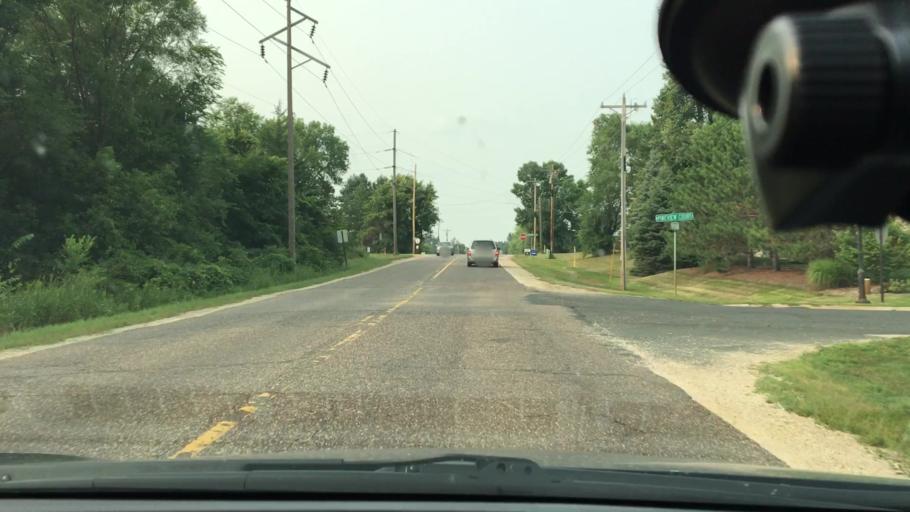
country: US
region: Minnesota
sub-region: Hennepin County
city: Champlin
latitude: 45.1981
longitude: -93.4425
